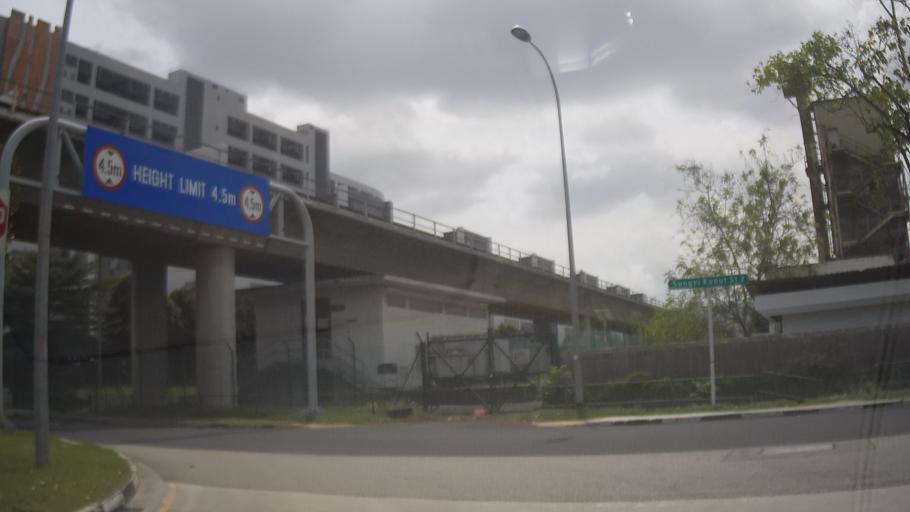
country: MY
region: Johor
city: Johor Bahru
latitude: 1.4126
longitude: 103.7488
